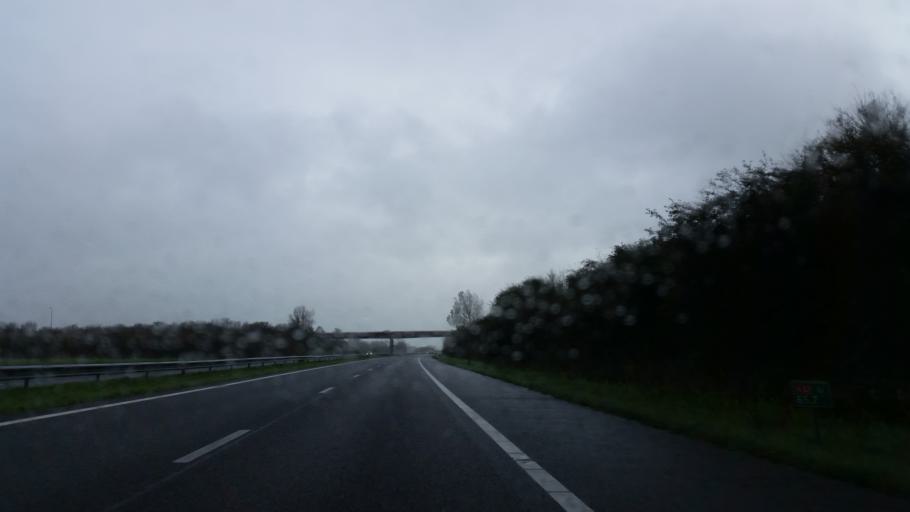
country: NL
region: Friesland
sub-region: Gemeente Boarnsterhim
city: Reduzum
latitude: 53.1140
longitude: 5.8118
